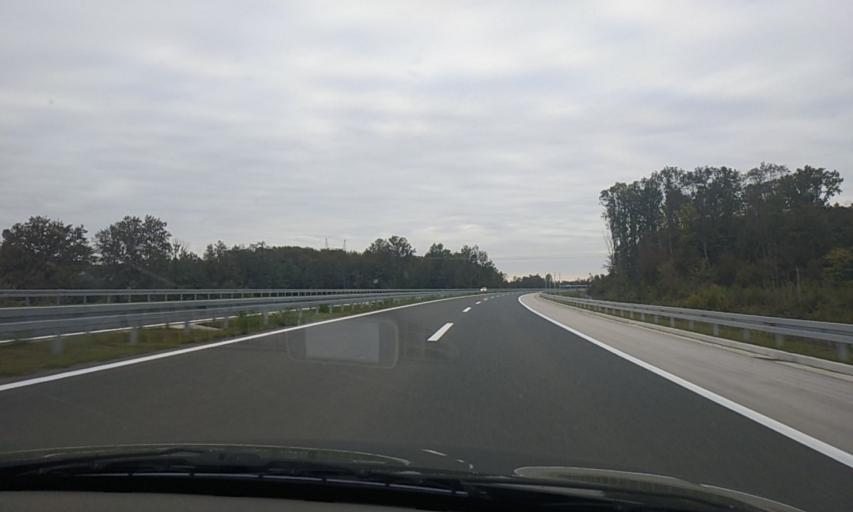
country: BA
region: Republika Srpska
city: Maglajani
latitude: 44.8873
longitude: 17.3733
